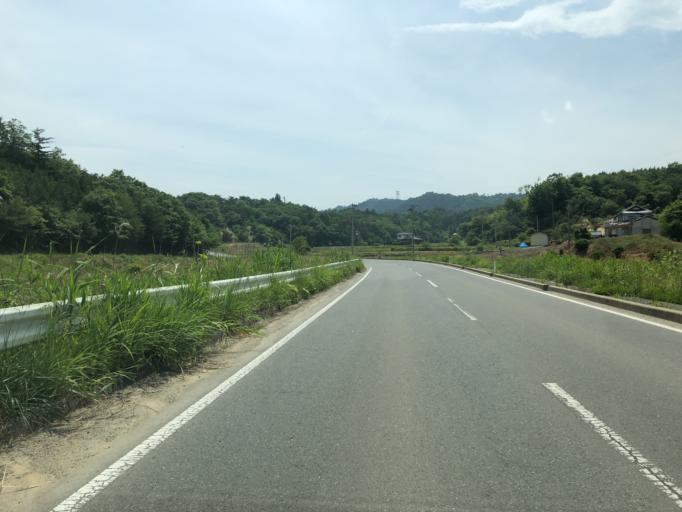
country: JP
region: Fukushima
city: Namie
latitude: 37.5589
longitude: 140.9271
